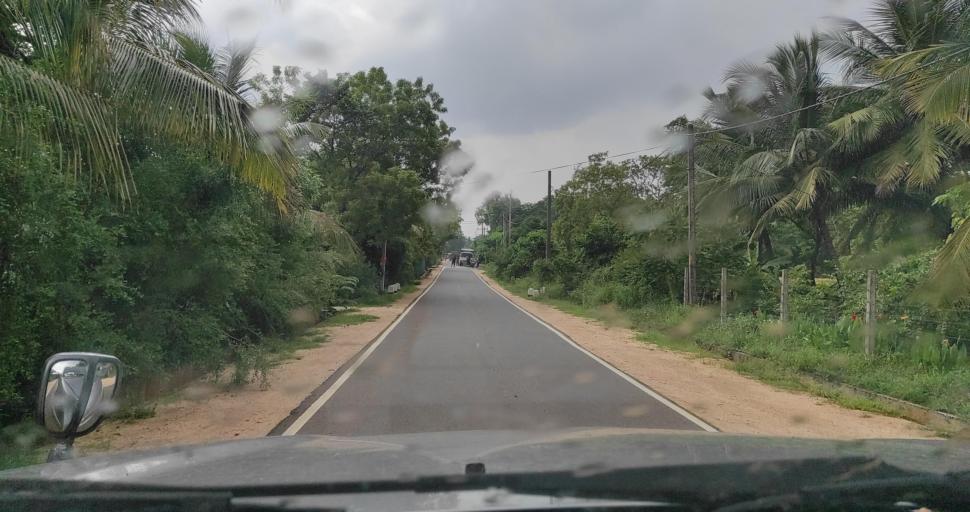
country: LK
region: Eastern Province
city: Trincomalee
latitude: 8.3689
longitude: 81.0098
